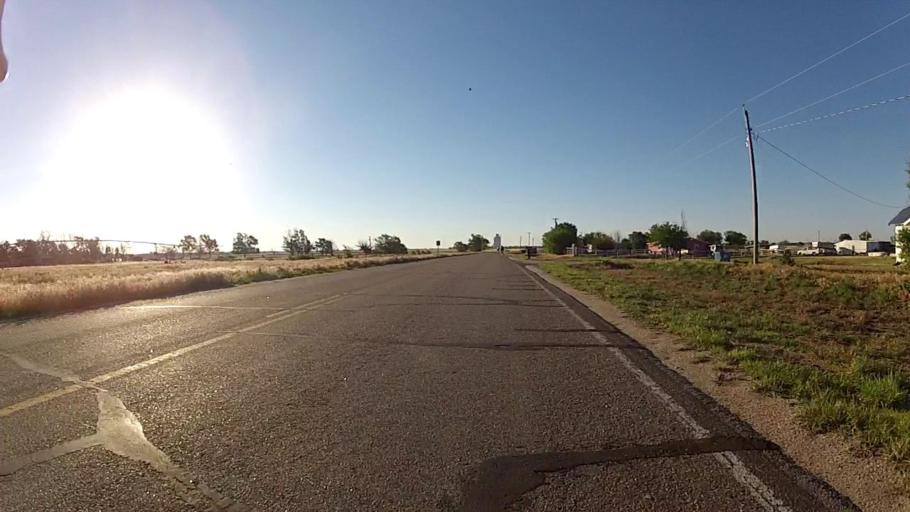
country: US
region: Kansas
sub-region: Ford County
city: Dodge City
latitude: 37.7075
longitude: -99.9089
